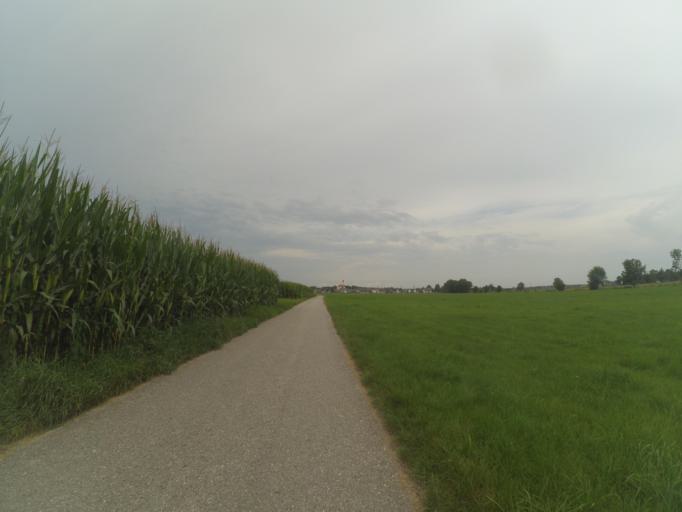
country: DE
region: Bavaria
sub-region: Swabia
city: Jengen
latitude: 48.0078
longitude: 10.7211
